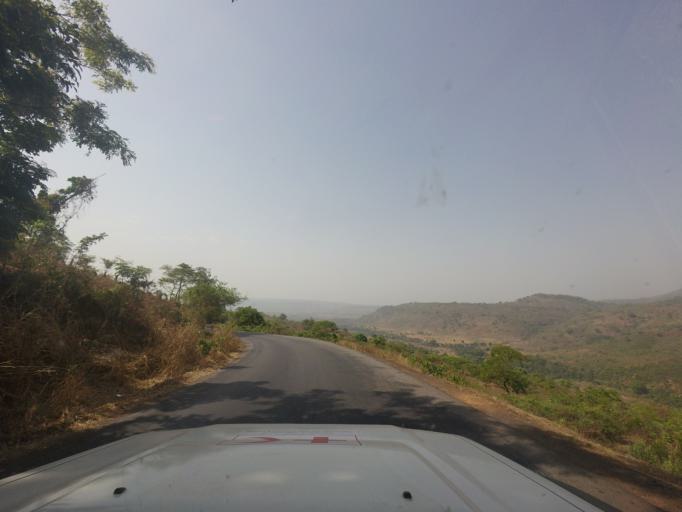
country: GN
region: Mamou
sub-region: Mamou Prefecture
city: Mamou
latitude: 10.2257
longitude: -12.4625
